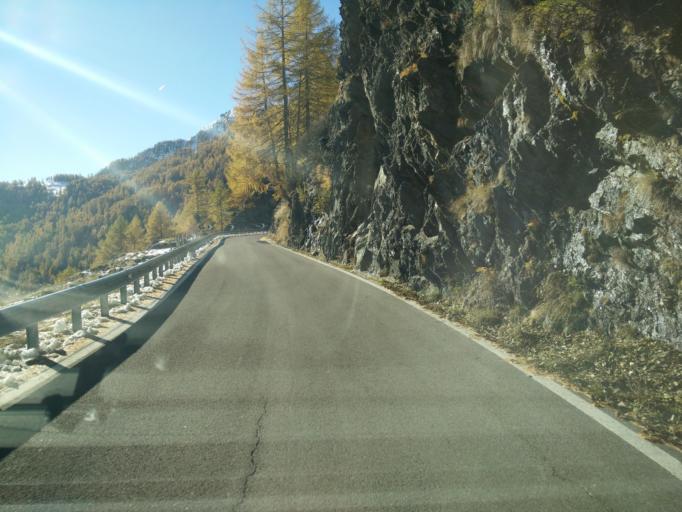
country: IT
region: Trentino-Alto Adige
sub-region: Bolzano
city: Moso in Passiria
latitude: 46.8899
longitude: 11.1272
